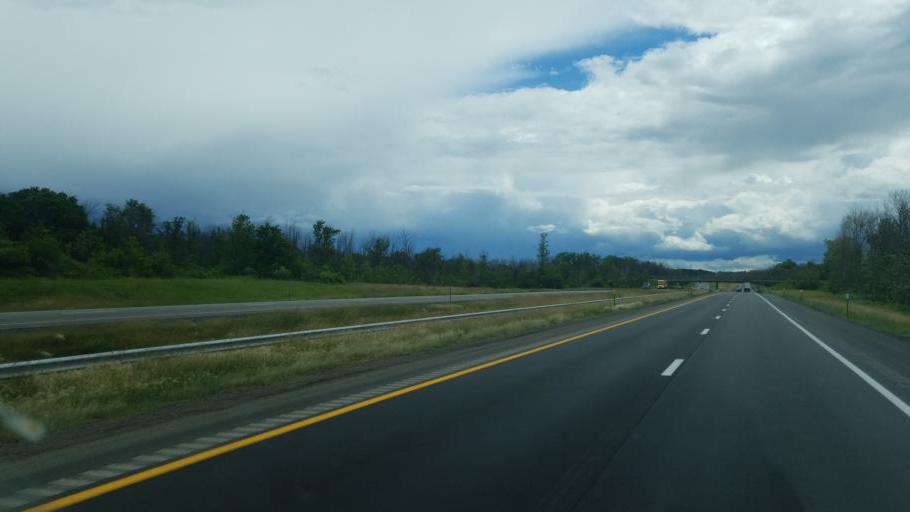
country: US
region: New York
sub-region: Livingston County
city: Caledonia
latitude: 43.0296
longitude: -77.8489
